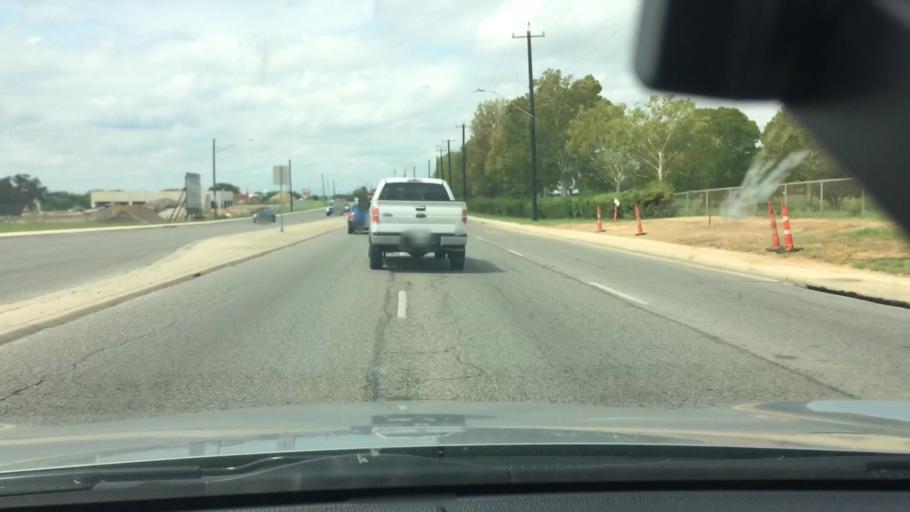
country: US
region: Texas
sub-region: Bexar County
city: San Antonio
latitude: 29.3519
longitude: -98.4535
